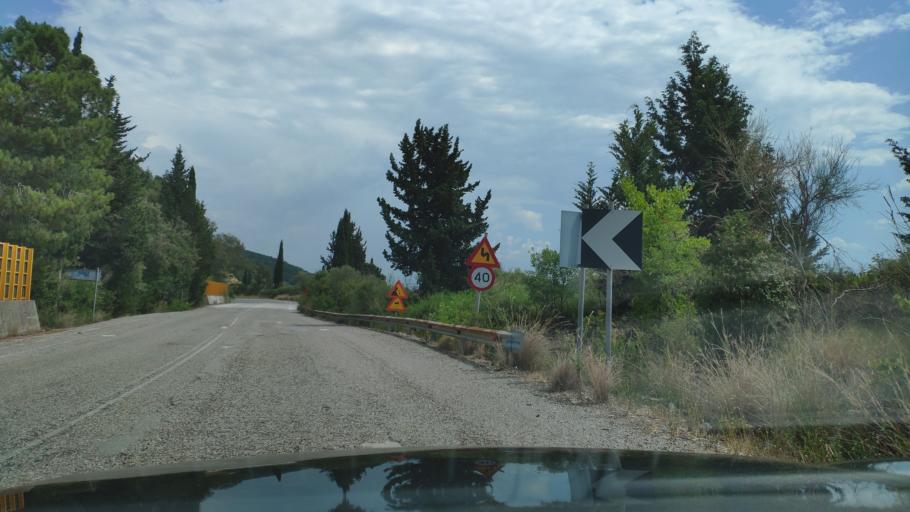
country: GR
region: West Greece
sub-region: Nomos Aitolias kai Akarnanias
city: Menidi
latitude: 39.0180
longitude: 21.1364
